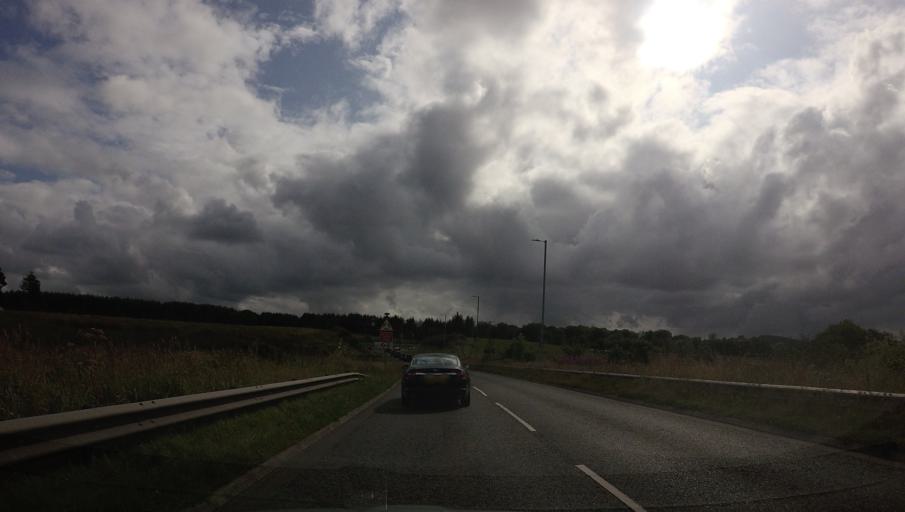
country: GB
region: Scotland
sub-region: Aberdeen City
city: Cults
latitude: 57.1476
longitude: -2.2009
